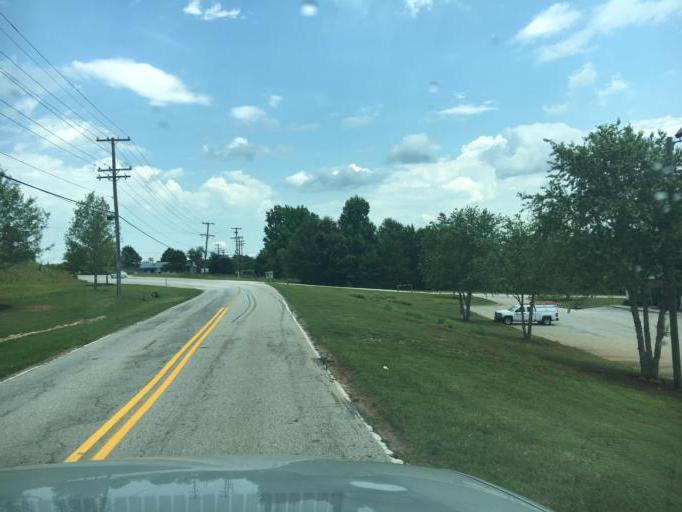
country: US
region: South Carolina
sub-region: Greenville County
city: Greer
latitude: 34.8721
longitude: -82.2322
